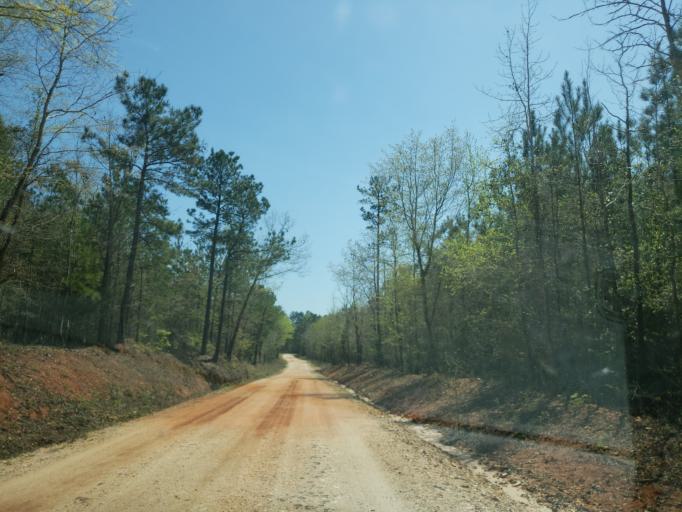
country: US
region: Alabama
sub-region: Tallapoosa County
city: Camp Hill
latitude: 32.6775
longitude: -85.6653
